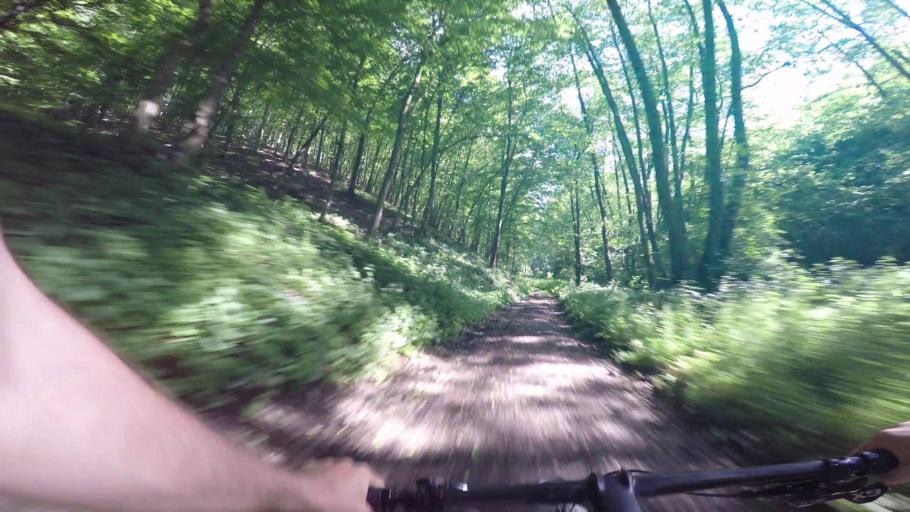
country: SK
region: Trnavsky
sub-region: Okres Trnava
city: Piestany
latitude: 48.6144
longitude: 17.9165
